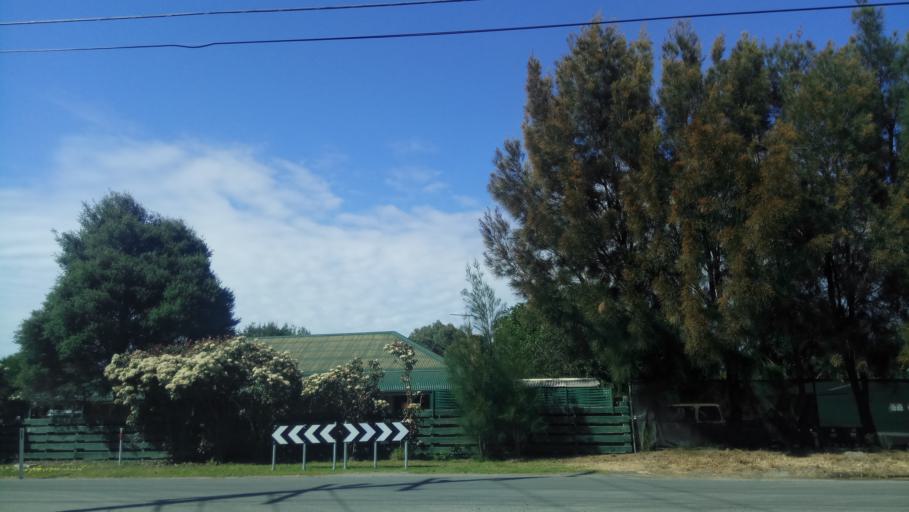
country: AU
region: Victoria
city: Heatherton
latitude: -37.9610
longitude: 145.0983
